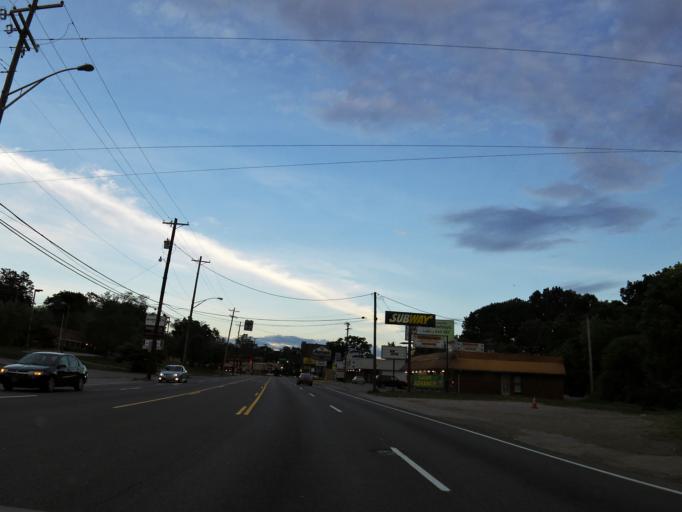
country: US
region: Tennessee
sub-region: Knox County
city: Knoxville
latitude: 35.9968
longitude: -83.9239
